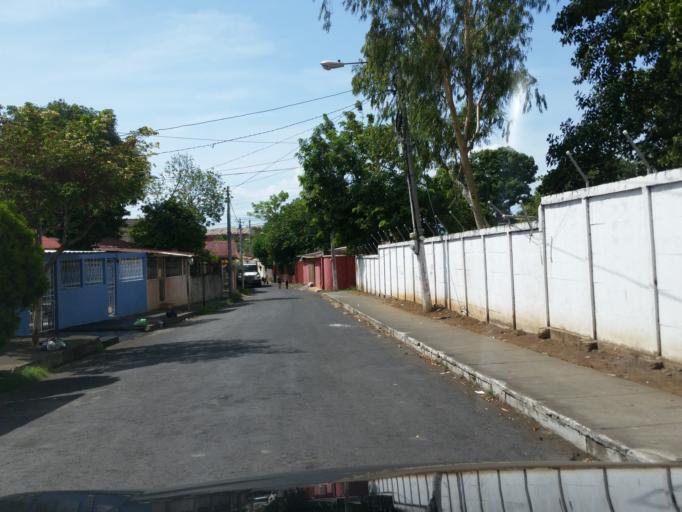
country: NI
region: Managua
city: Managua
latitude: 12.1443
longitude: -86.2492
